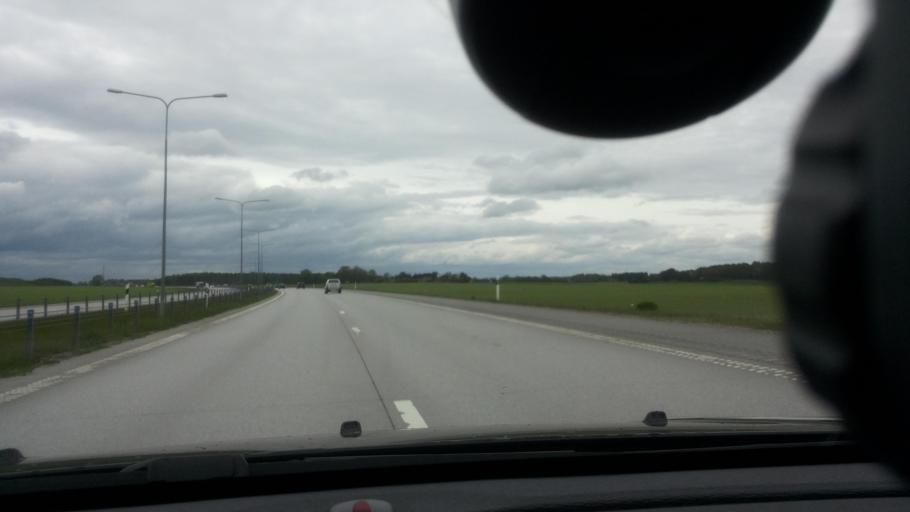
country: SE
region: Uppsala
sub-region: Uppsala Kommun
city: Saevja
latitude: 59.8558
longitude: 17.7311
